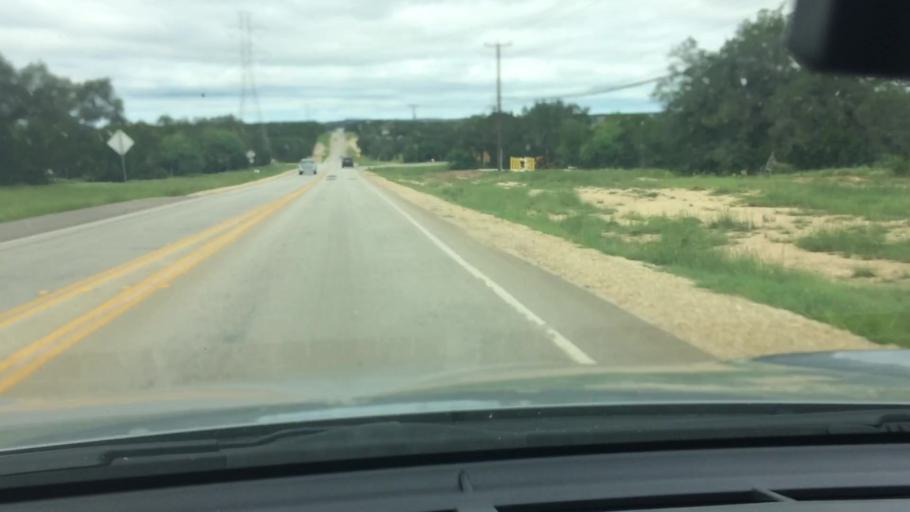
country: US
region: Texas
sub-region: Comal County
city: Garden Ridge
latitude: 29.6411
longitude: -98.3804
